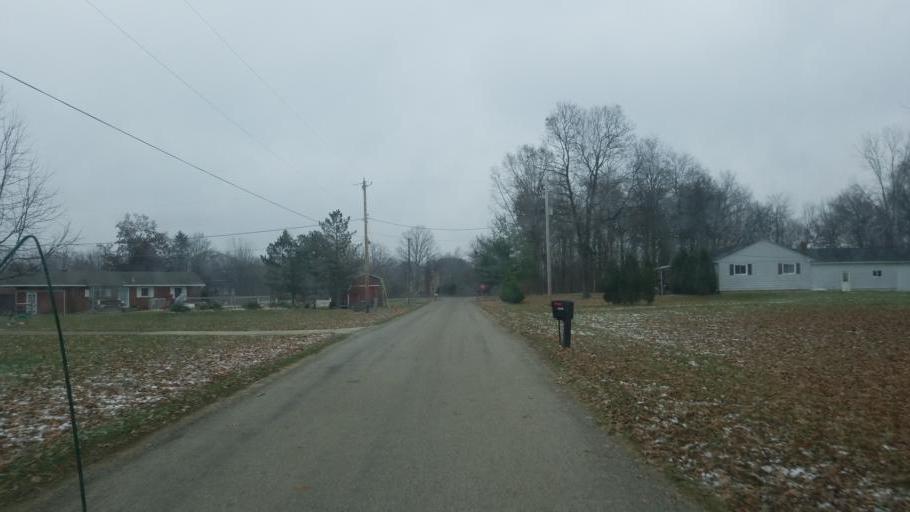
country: US
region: Ohio
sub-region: Huron County
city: New London
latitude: 40.9755
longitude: -82.3696
